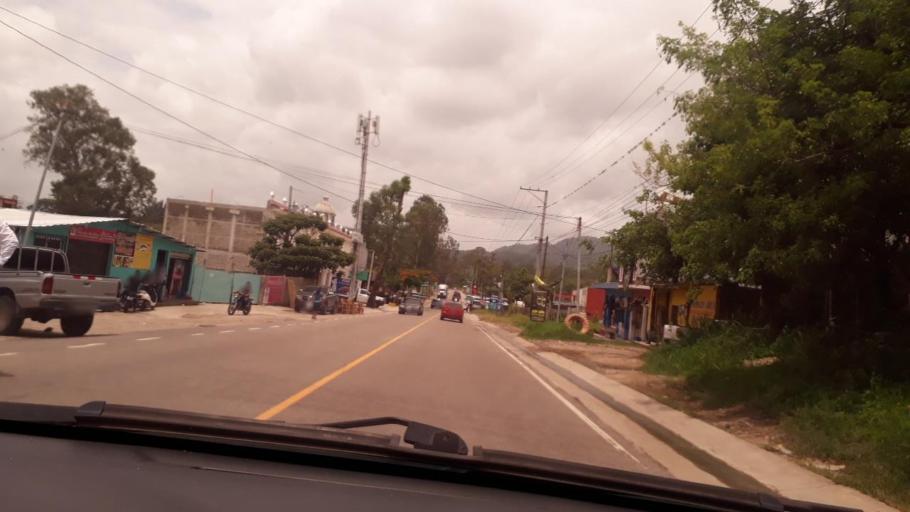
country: GT
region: Chiquimula
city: Esquipulas
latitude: 14.5610
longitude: -89.3540
